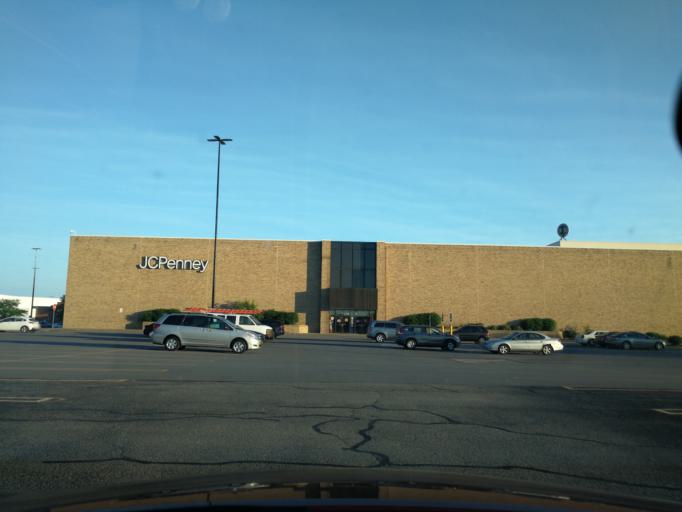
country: US
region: New York
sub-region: Monroe County
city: Rochester
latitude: 43.0864
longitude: -77.6336
